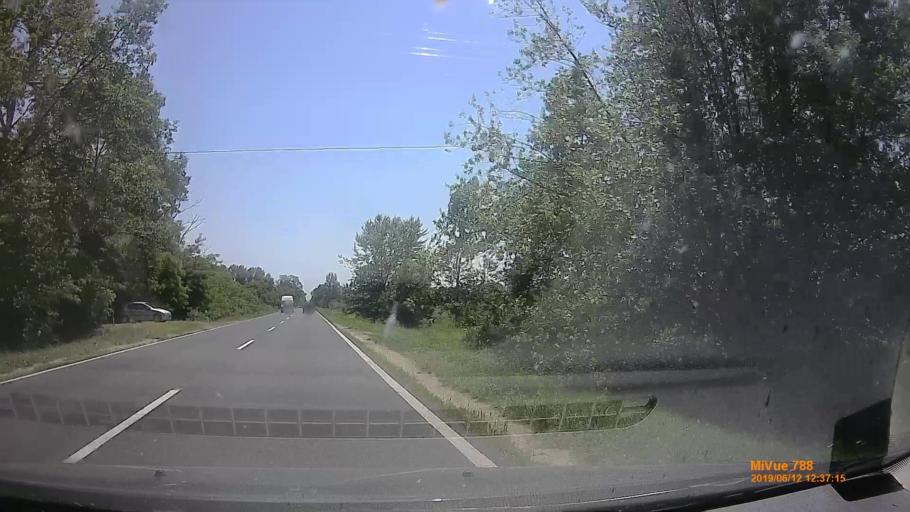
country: HU
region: Bacs-Kiskun
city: Varosfoeld
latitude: 46.7888
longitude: 19.7902
